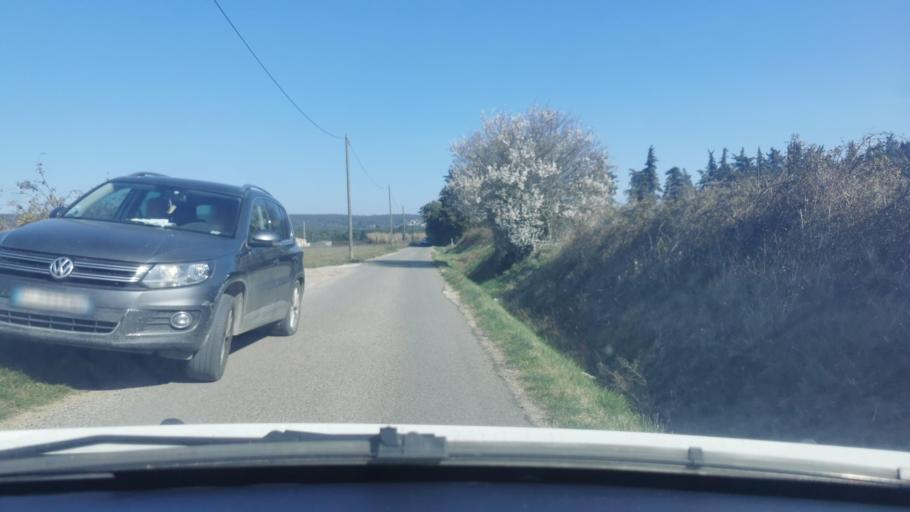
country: FR
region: Languedoc-Roussillon
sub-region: Departement du Gard
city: Montaren-et-Saint-Mediers
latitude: 44.0377
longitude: 4.3897
